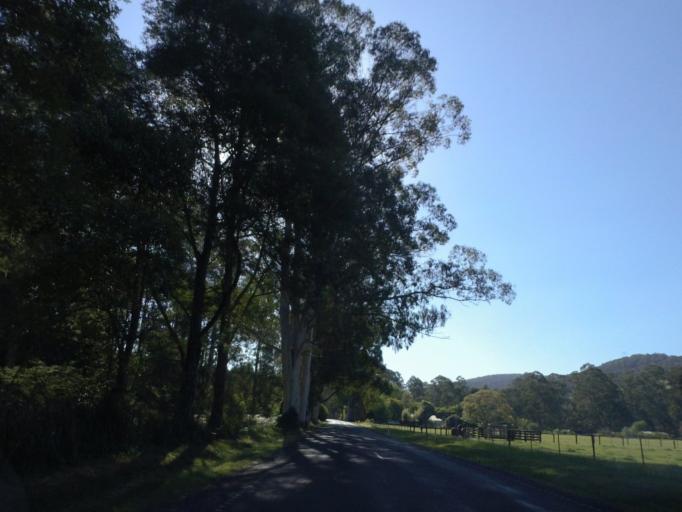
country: AU
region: Victoria
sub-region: Yarra Ranges
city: Millgrove
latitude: -37.8566
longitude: 145.7227
